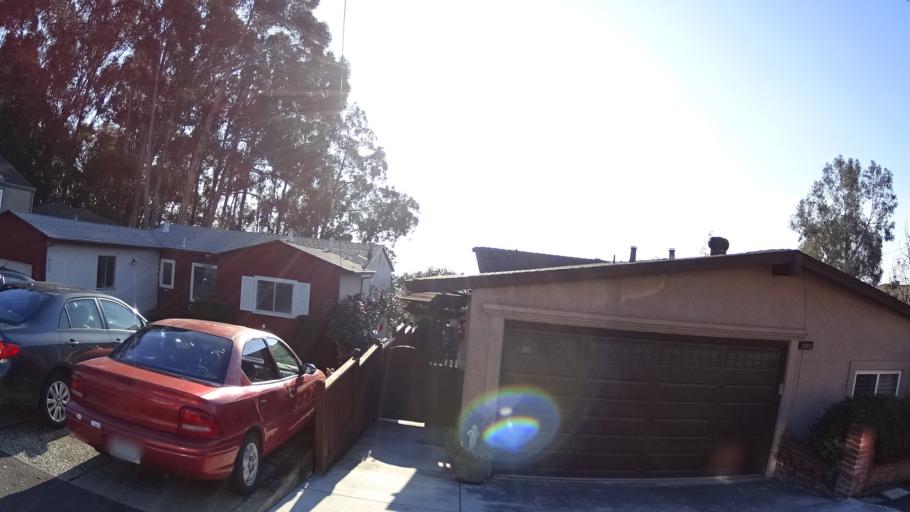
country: US
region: California
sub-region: Alameda County
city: Hayward
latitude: 37.6539
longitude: -122.0640
